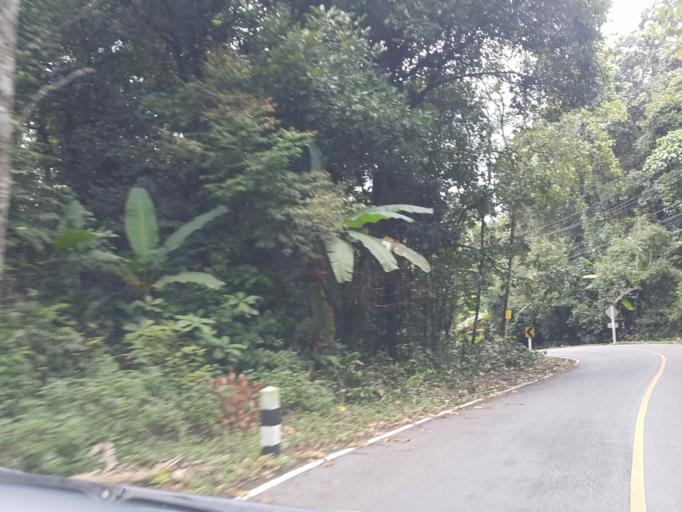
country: TH
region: Chiang Mai
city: Mae Chaem
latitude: 18.5238
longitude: 98.4873
